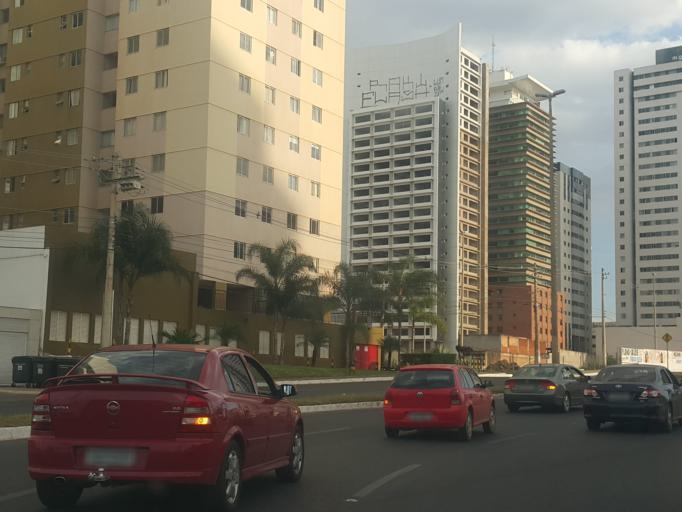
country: BR
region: Federal District
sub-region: Brasilia
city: Brasilia
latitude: -15.8331
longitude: -48.0393
